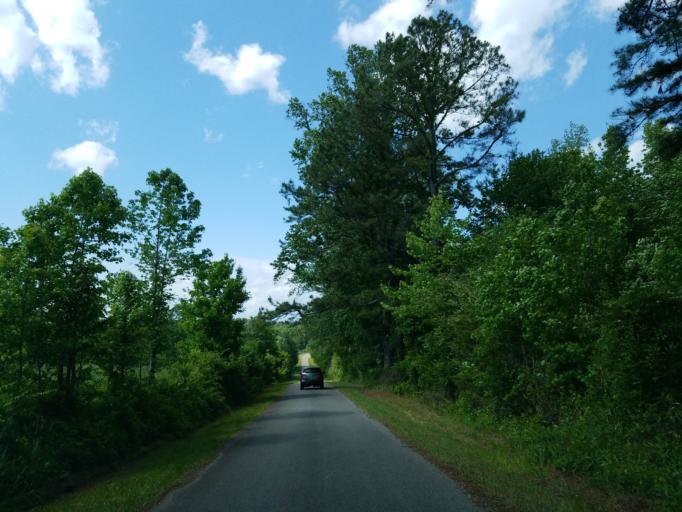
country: US
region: Georgia
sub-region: Cherokee County
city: Ball Ground
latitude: 34.2738
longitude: -84.3120
